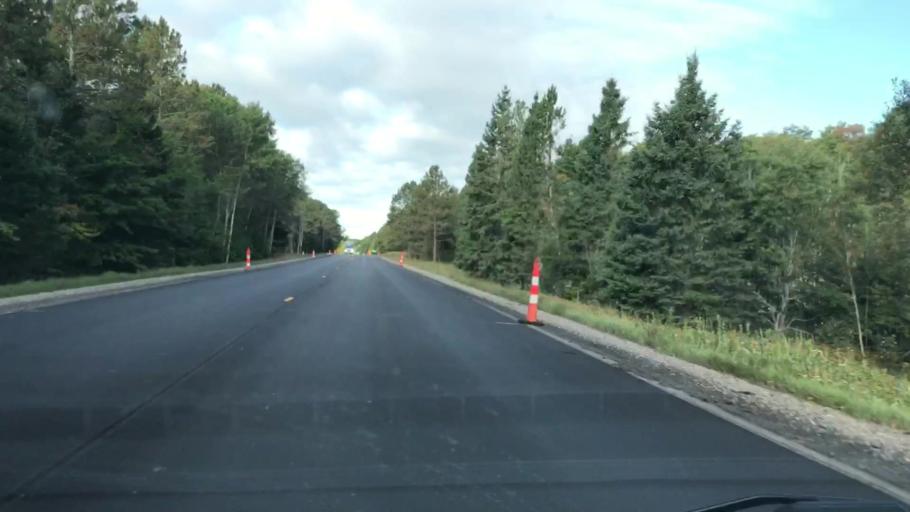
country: US
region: Michigan
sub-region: Luce County
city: Newberry
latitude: 46.3464
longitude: -85.0159
